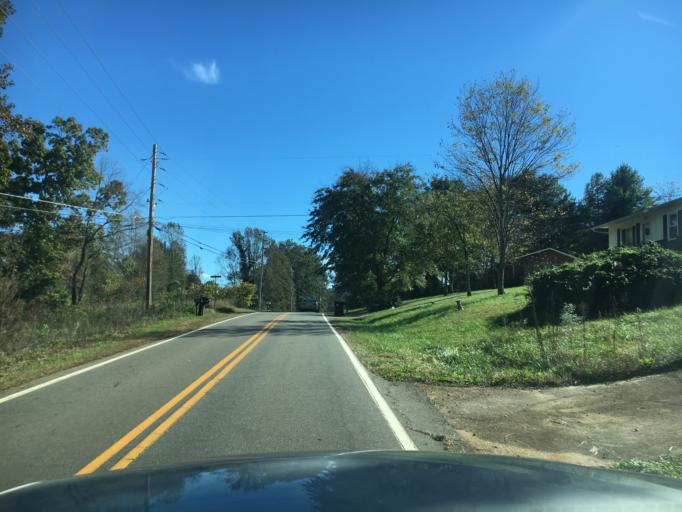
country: US
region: North Carolina
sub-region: Burke County
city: Salem
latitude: 35.7105
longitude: -81.7361
